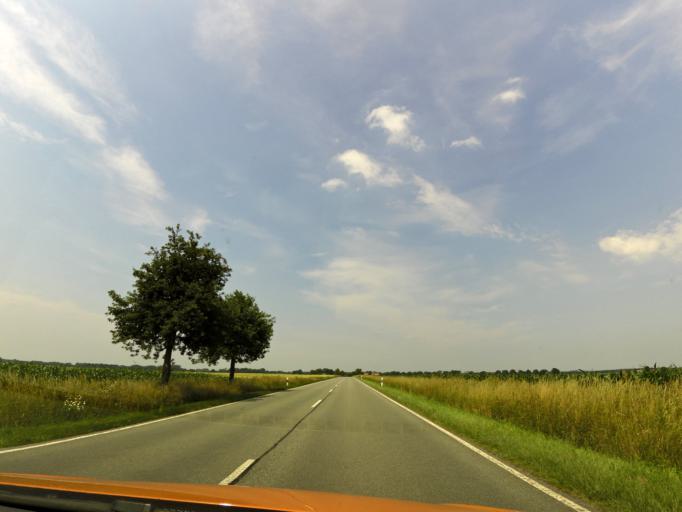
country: DE
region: Brandenburg
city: Kyritz
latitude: 52.9998
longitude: 12.3371
